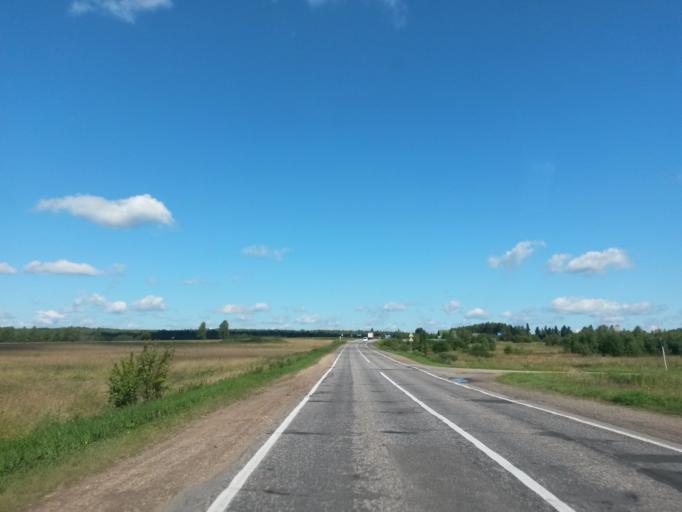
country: RU
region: Jaroslavl
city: Krasnyye Tkachi
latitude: 57.4573
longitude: 39.9103
